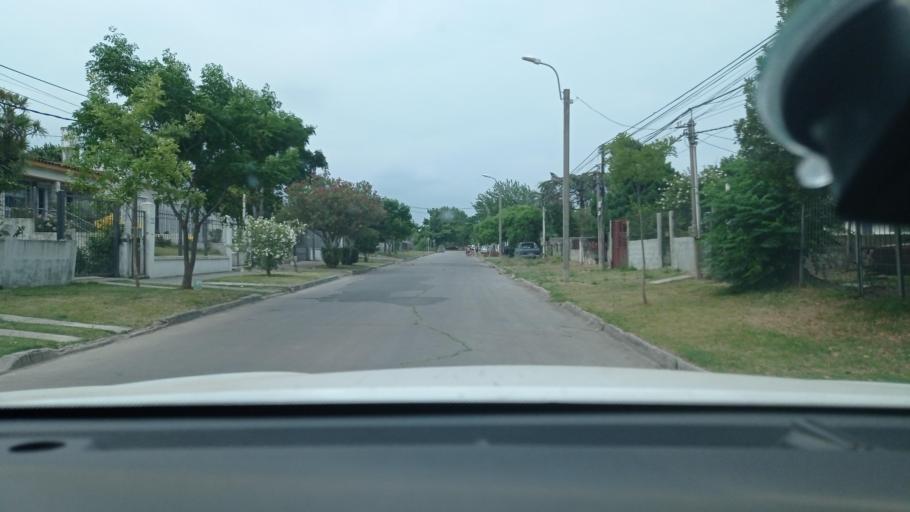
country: UY
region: Canelones
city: Paso de Carrasco
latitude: -34.8725
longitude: -56.0890
